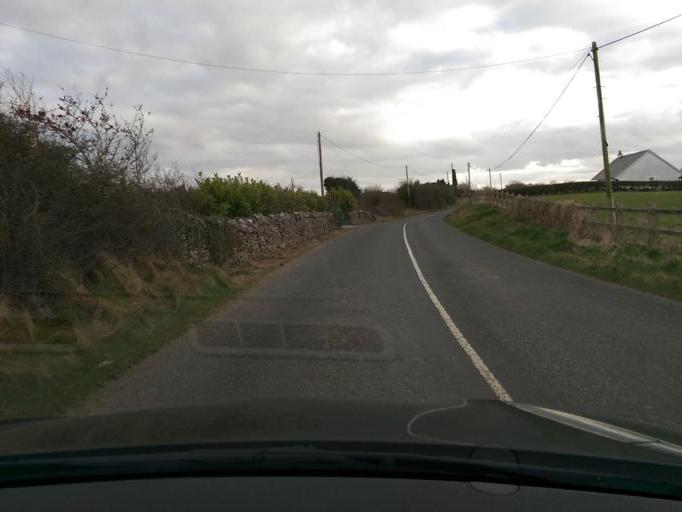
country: IE
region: Leinster
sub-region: Uibh Fhaili
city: Banagher
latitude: 53.3022
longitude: -8.0092
